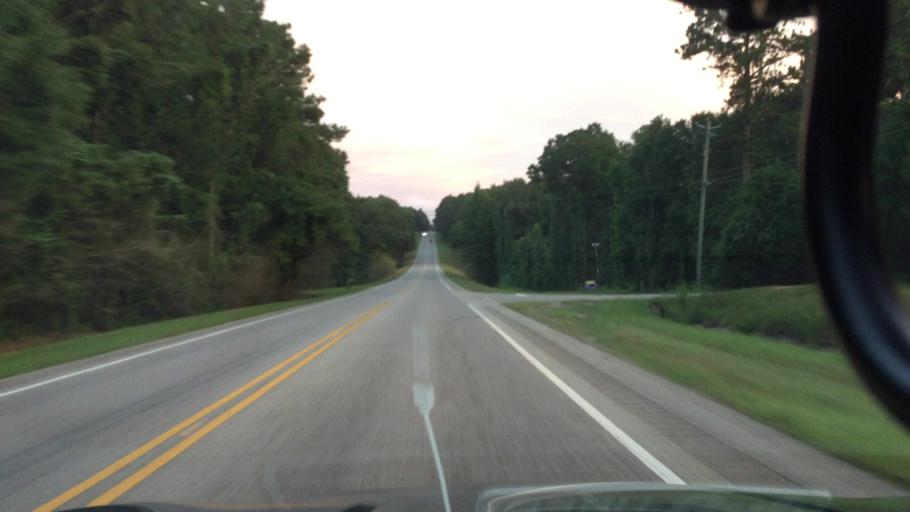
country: US
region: Alabama
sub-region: Coffee County
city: New Brockton
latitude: 31.3858
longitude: -85.8751
